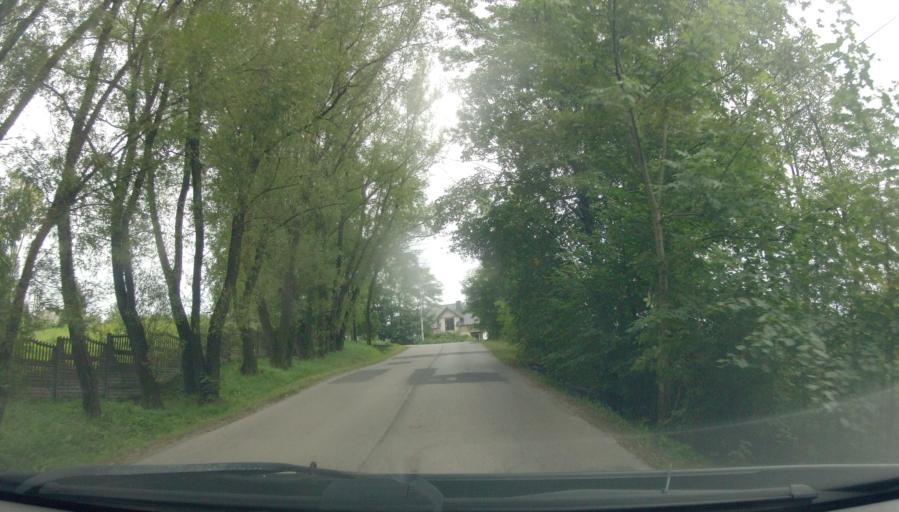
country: PL
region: Lesser Poland Voivodeship
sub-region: Powiat krakowski
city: Ochojno
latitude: 49.9438
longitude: 19.9974
